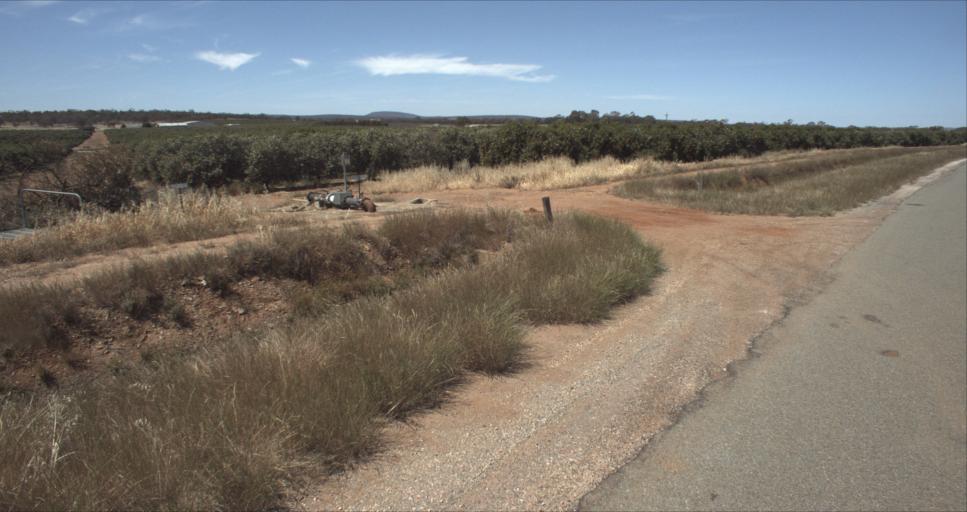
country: AU
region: New South Wales
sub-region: Leeton
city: Leeton
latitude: -34.5934
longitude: 146.4734
